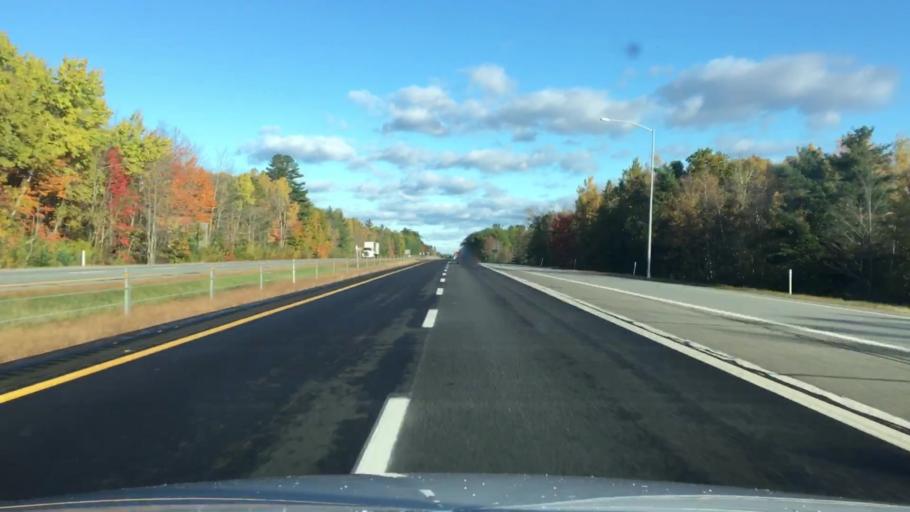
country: US
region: Maine
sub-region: Penobscot County
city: Orono
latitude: 44.9055
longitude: -68.6931
